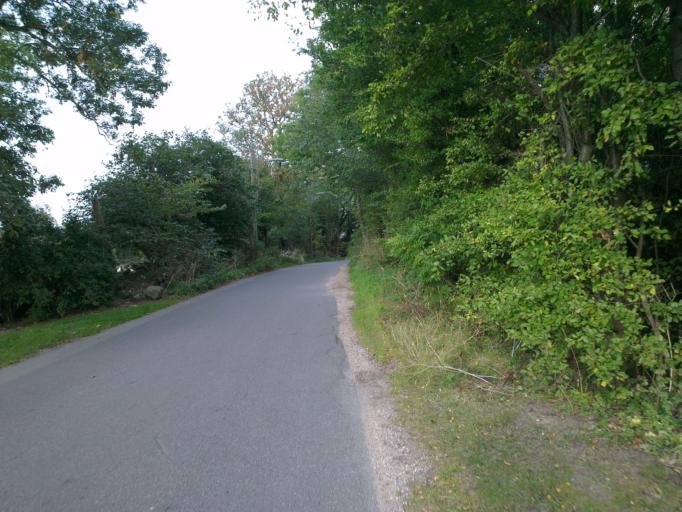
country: DK
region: Capital Region
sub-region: Frederikssund Kommune
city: Frederikssund
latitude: 55.8102
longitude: 12.0262
